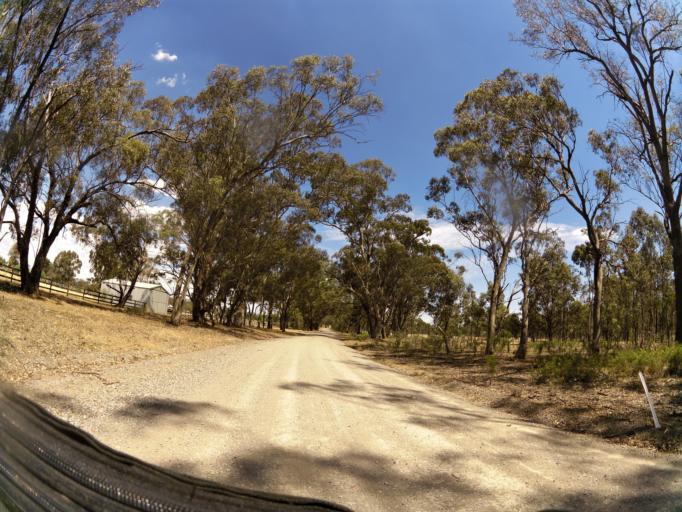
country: AU
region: Victoria
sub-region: Campaspe
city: Kyabram
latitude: -36.8128
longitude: 145.0781
